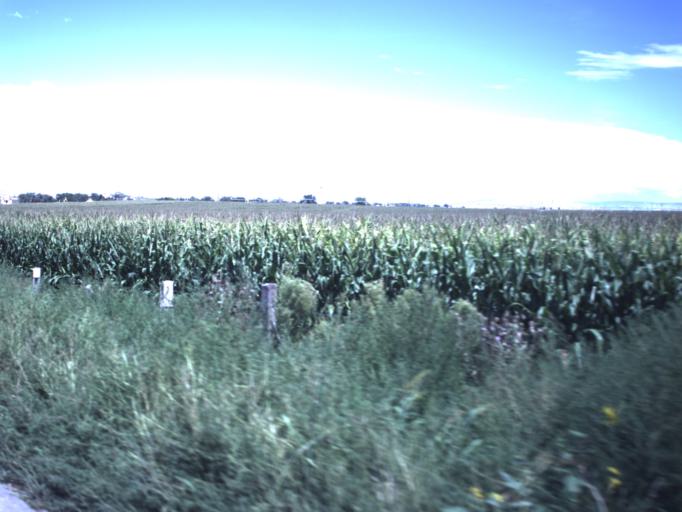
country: US
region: Utah
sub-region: Uintah County
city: Naples
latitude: 40.1777
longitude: -109.6645
